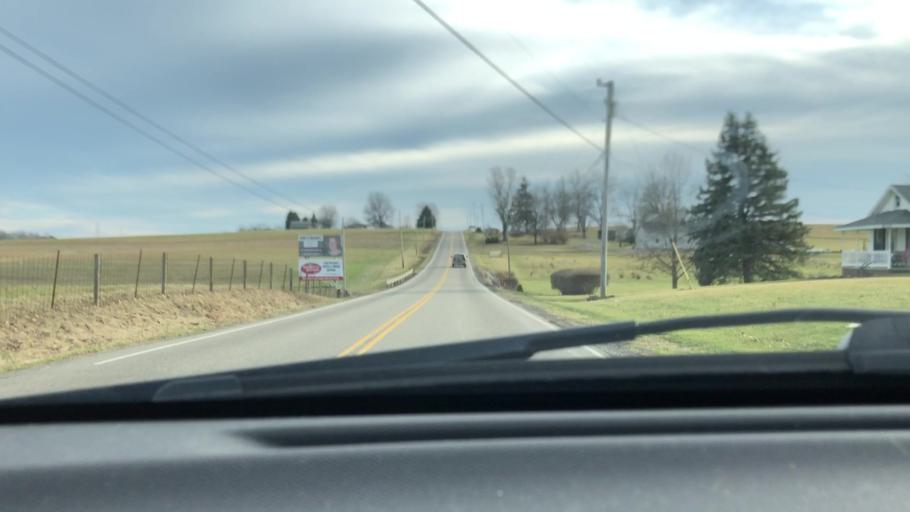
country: US
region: Ohio
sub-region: Wayne County
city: Dalton
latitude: 40.7780
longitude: -81.7453
